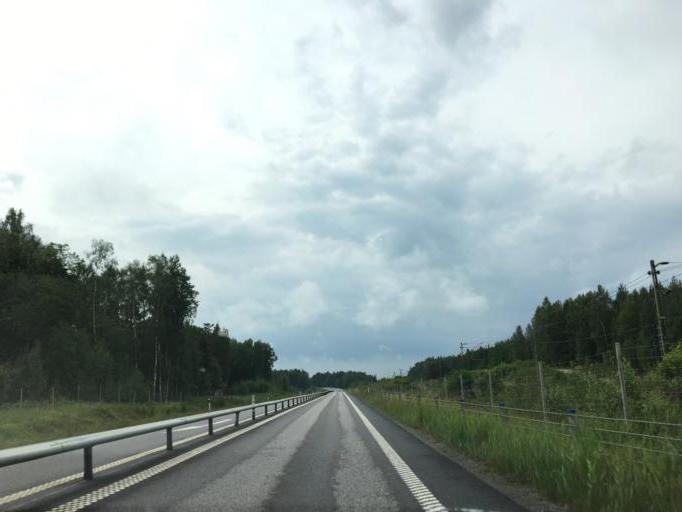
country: SE
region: Soedermanland
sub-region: Katrineholms Kommun
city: Katrineholm
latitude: 58.9158
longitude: 16.1977
